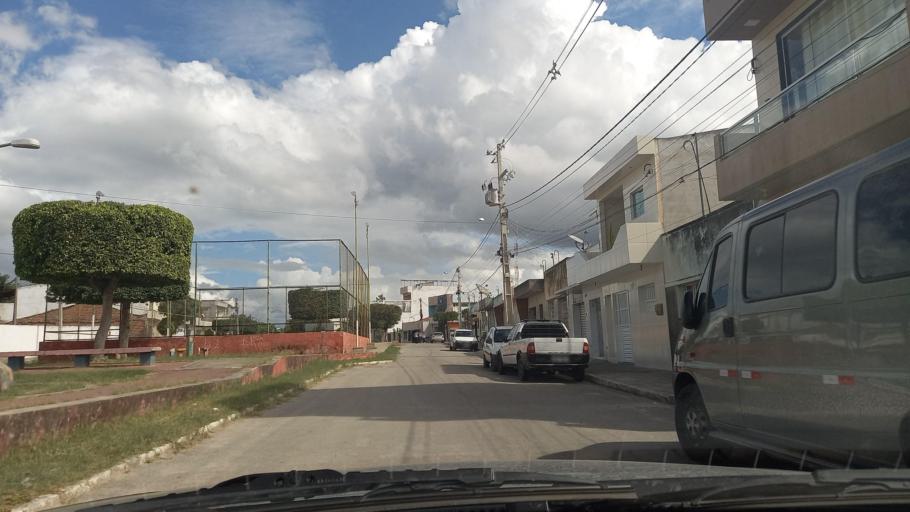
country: BR
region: Pernambuco
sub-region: Cachoeirinha
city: Cachoeirinha
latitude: -8.4919
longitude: -36.2382
